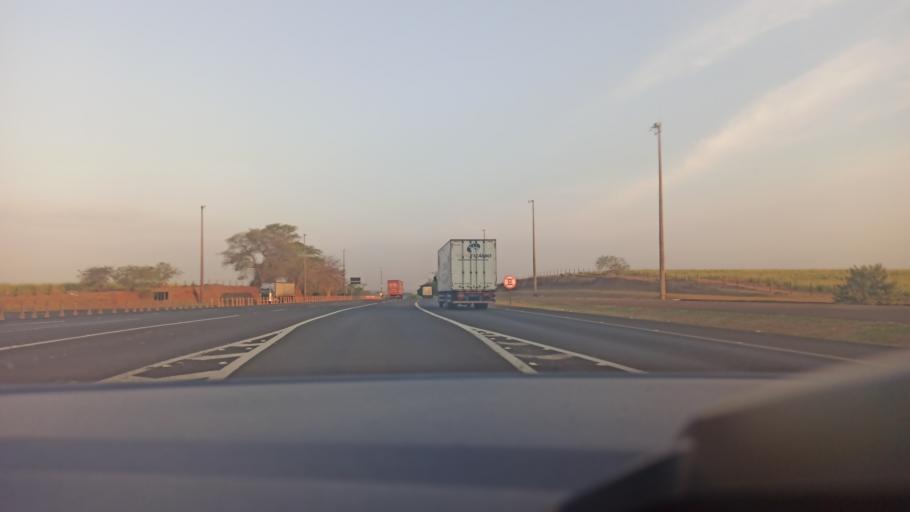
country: BR
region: Sao Paulo
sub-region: Santa Adelia
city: Santa Adelia
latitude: -21.3835
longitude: -48.7313
